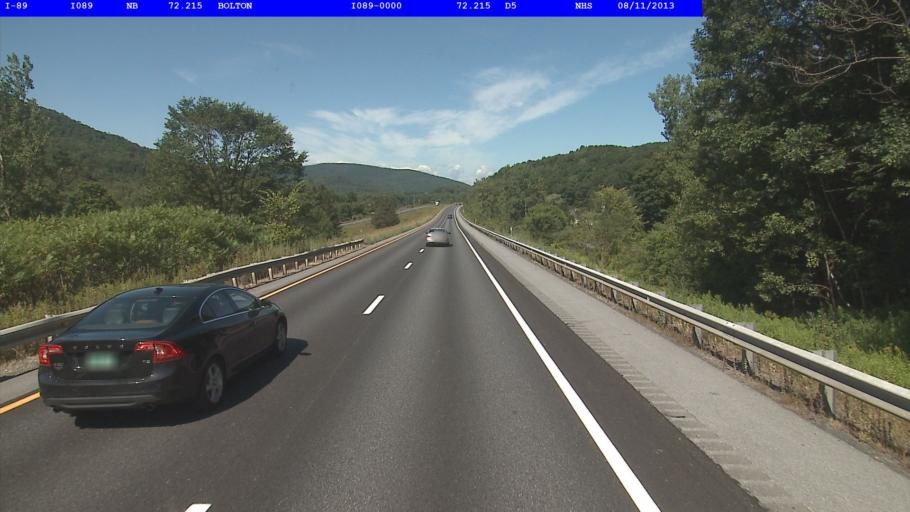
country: US
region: Vermont
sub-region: Chittenden County
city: Jericho
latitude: 44.3799
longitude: -72.9102
